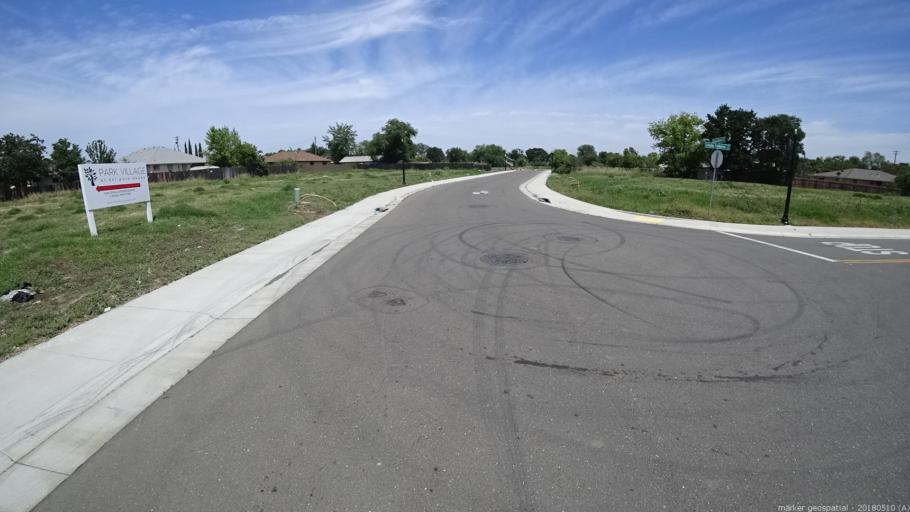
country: US
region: California
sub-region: Sacramento County
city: Rio Linda
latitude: 38.6299
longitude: -121.4509
